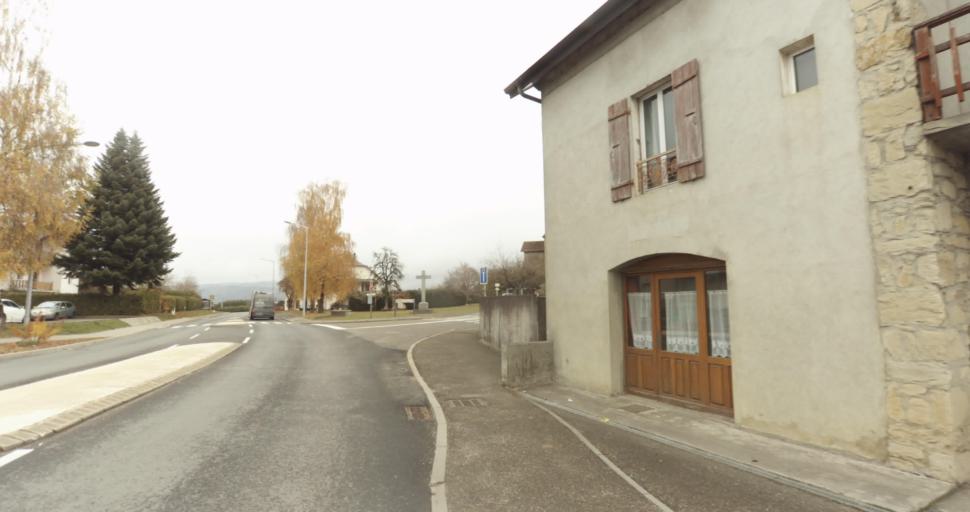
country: FR
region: Rhone-Alpes
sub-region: Departement de la Haute-Savoie
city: Groisy
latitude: 46.0095
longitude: 6.1703
